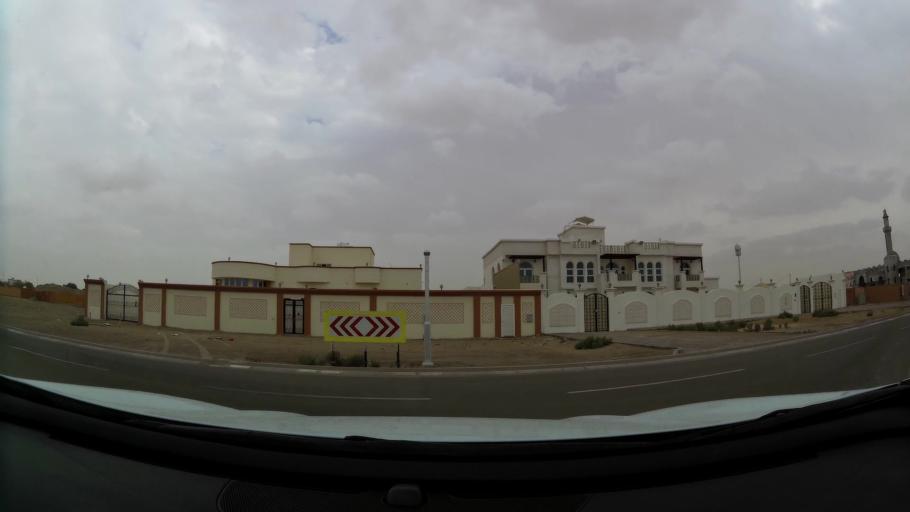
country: AE
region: Abu Dhabi
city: Abu Dhabi
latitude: 24.3538
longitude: 54.6574
